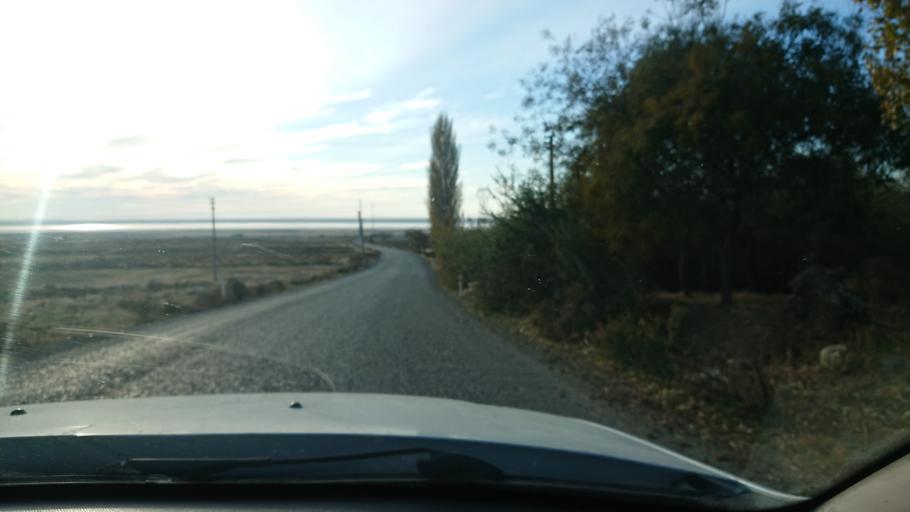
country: TR
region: Ankara
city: Sereflikochisar
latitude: 38.7449
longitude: 33.6798
